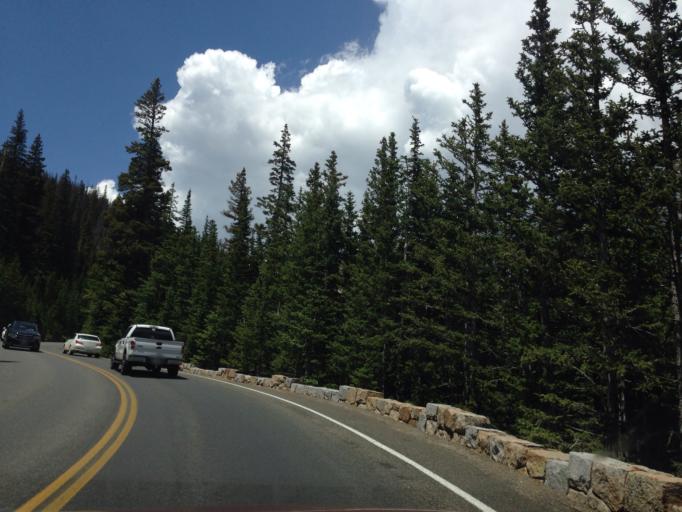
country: US
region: Colorado
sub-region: Larimer County
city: Estes Park
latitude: 40.3857
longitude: -105.6649
